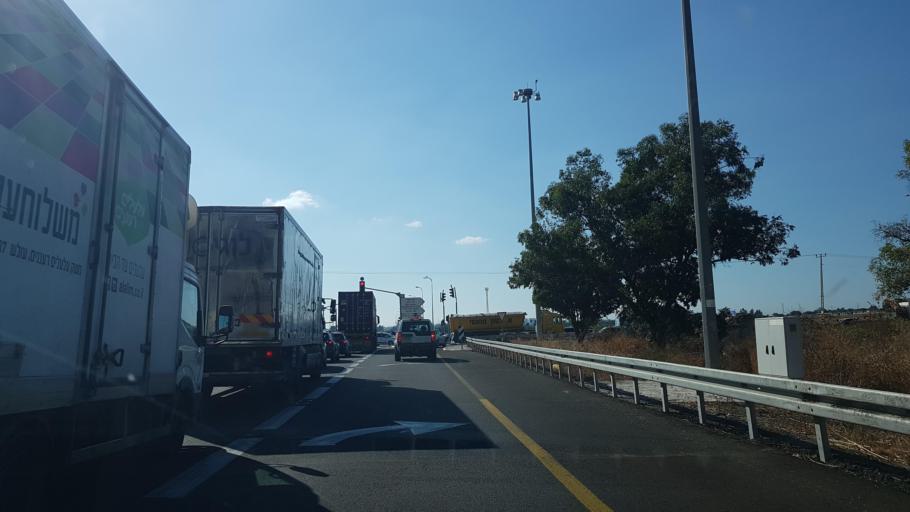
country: PS
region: West Bank
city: Tulkarm
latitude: 32.3120
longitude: 35.0003
